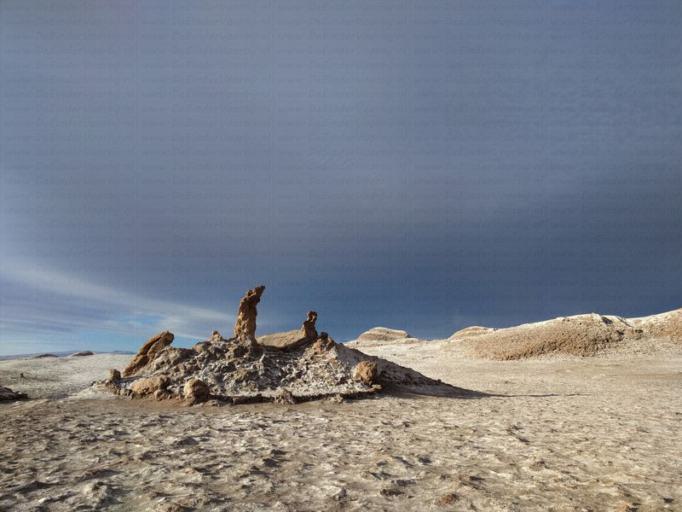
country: CL
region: Antofagasta
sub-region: Provincia de El Loa
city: San Pedro de Atacama
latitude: -22.9198
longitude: -68.3193
